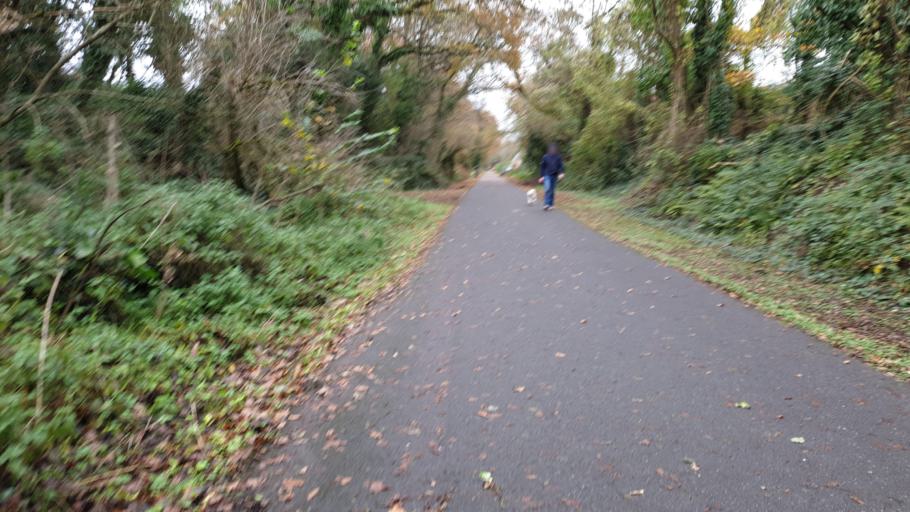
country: IE
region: Munster
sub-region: County Cork
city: Passage West
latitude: 51.8840
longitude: -8.4048
